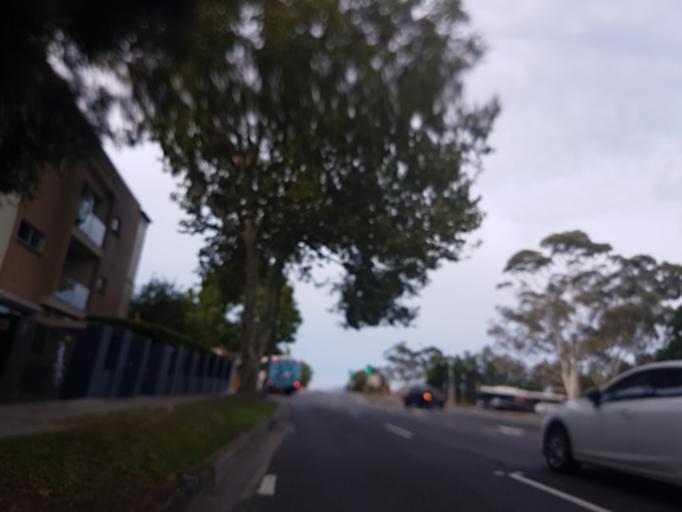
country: AU
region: New South Wales
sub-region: North Sydney
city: Cammeray
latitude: -33.8254
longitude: 151.2096
